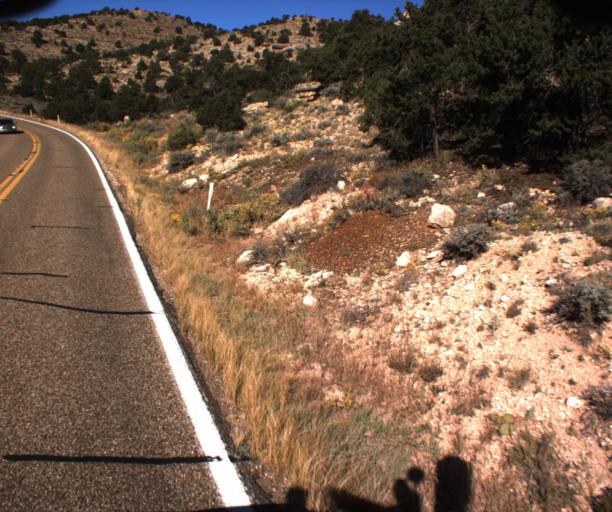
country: US
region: Arizona
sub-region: Coconino County
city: Fredonia
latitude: 36.7253
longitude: -112.0747
